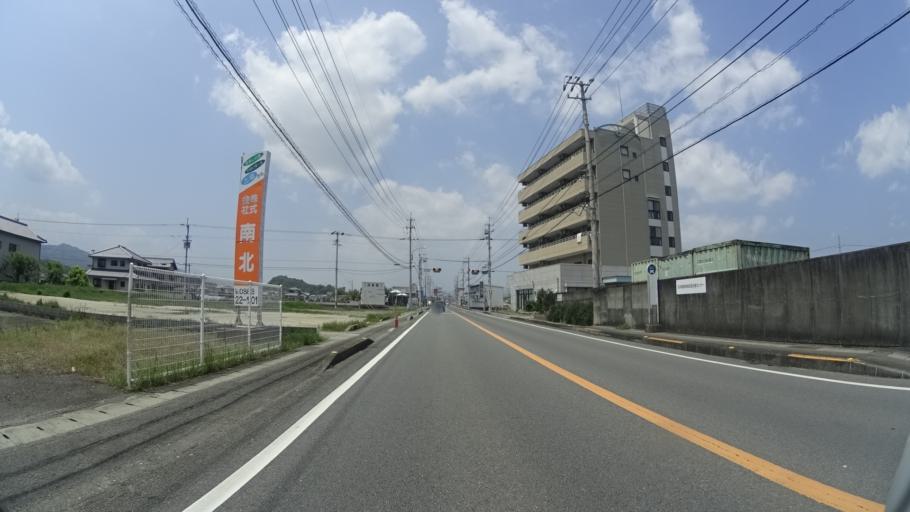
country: JP
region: Tokushima
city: Ishii
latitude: 34.0703
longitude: 134.4047
